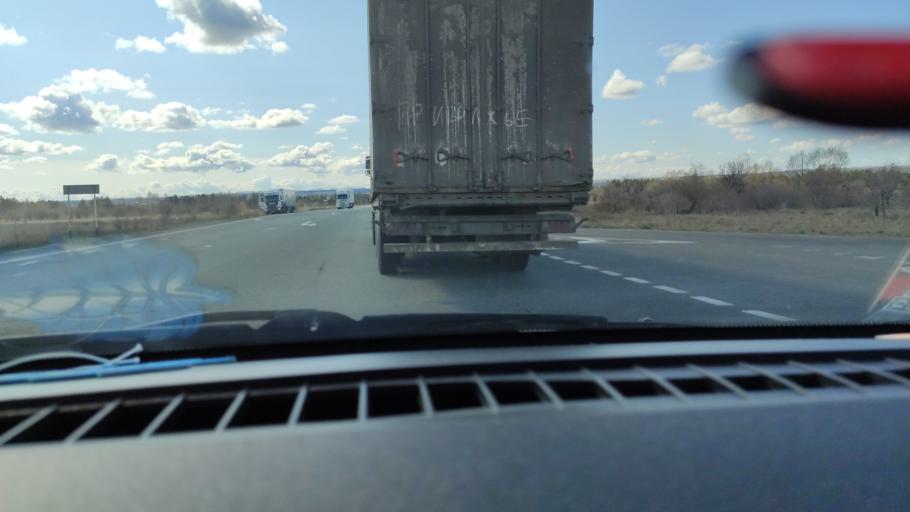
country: RU
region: Samara
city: Varlamovo
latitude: 53.1544
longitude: 48.2840
